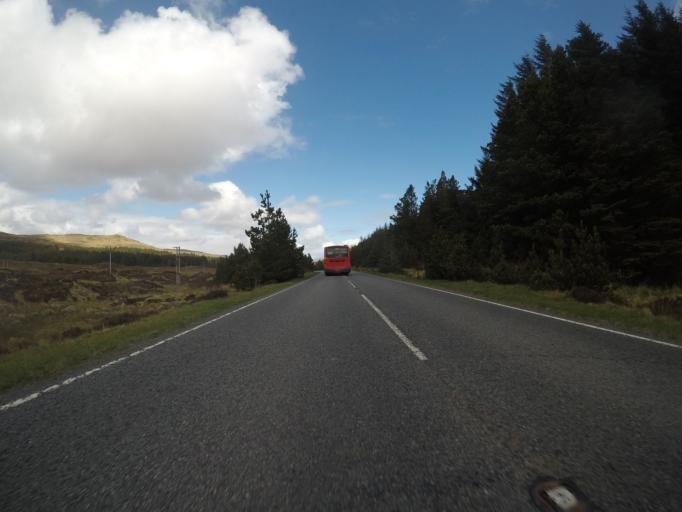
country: GB
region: Scotland
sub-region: Highland
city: Isle of Skye
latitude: 57.3244
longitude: -6.2043
